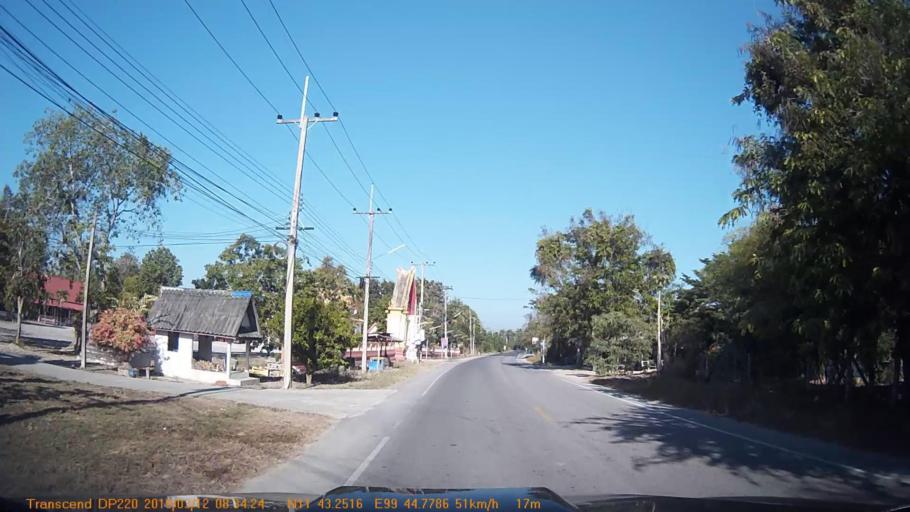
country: TH
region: Prachuap Khiri Khan
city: Prachuap Khiri Khan
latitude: 11.7209
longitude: 99.7461
